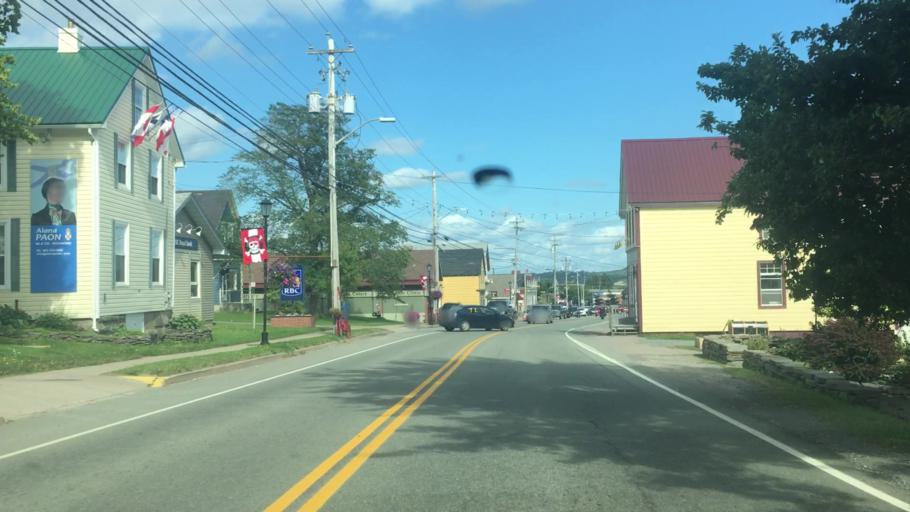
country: CA
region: Nova Scotia
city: Princeville
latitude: 45.6553
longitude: -60.8779
